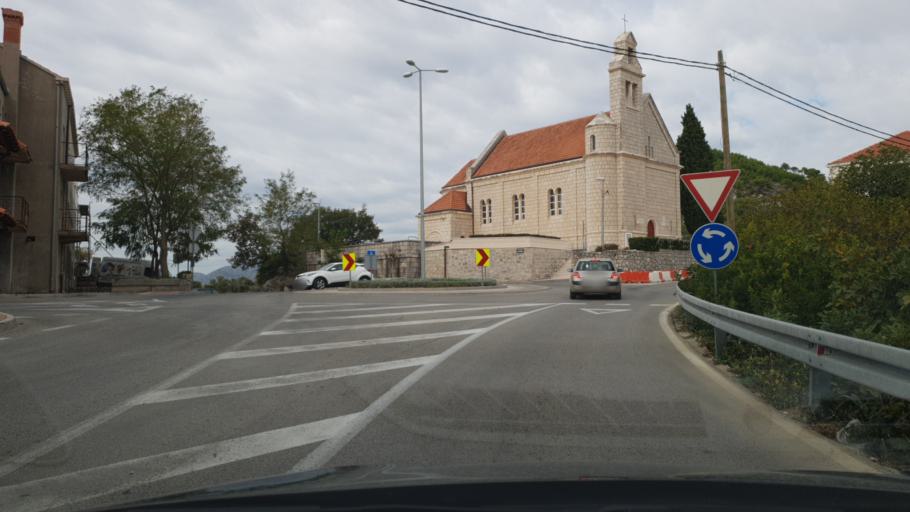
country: HR
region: Dubrovacko-Neretvanska
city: Cibaca
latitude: 42.6437
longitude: 18.1586
